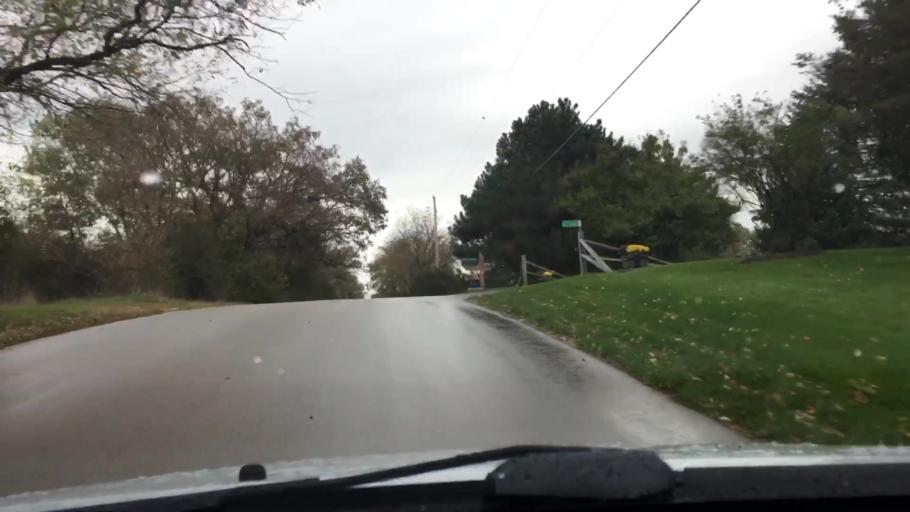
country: US
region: Wisconsin
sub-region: Waukesha County
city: North Prairie
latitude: 42.9303
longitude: -88.4388
